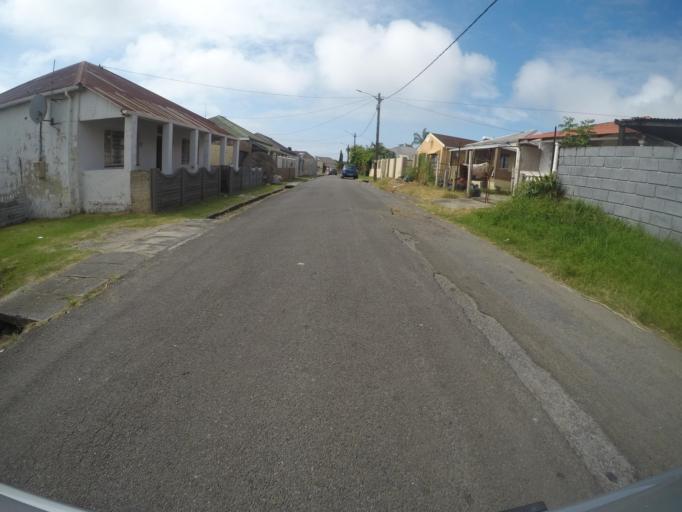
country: ZA
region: Eastern Cape
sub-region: Buffalo City Metropolitan Municipality
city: East London
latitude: -32.9976
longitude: 27.9083
